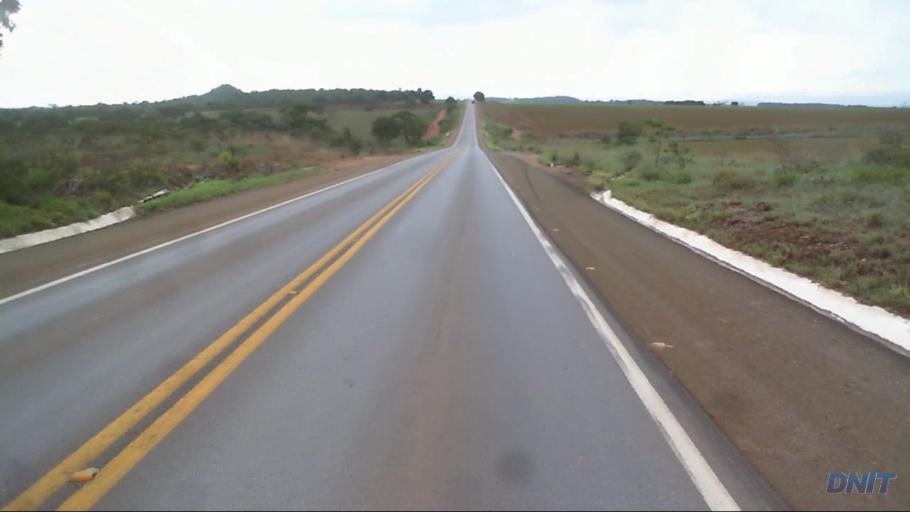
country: BR
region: Goias
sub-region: Uruacu
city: Uruacu
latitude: -14.6556
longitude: -49.1588
